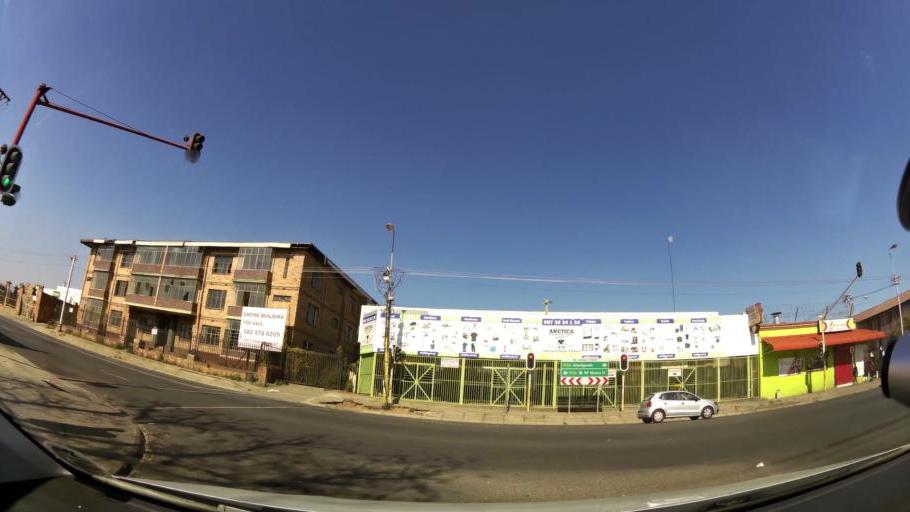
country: ZA
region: Gauteng
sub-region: City of Tshwane Metropolitan Municipality
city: Pretoria
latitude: -25.7490
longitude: 28.1502
